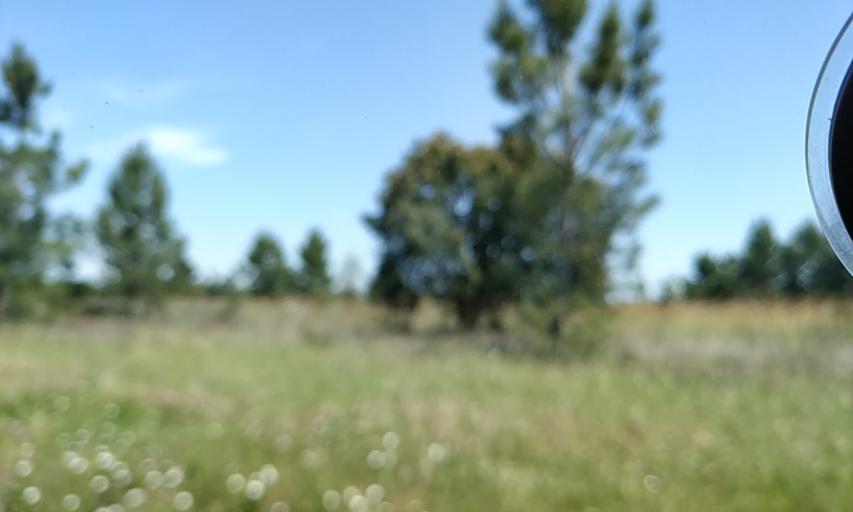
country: PT
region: Setubal
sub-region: Palmela
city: Palmela
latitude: 38.6237
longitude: -8.7466
